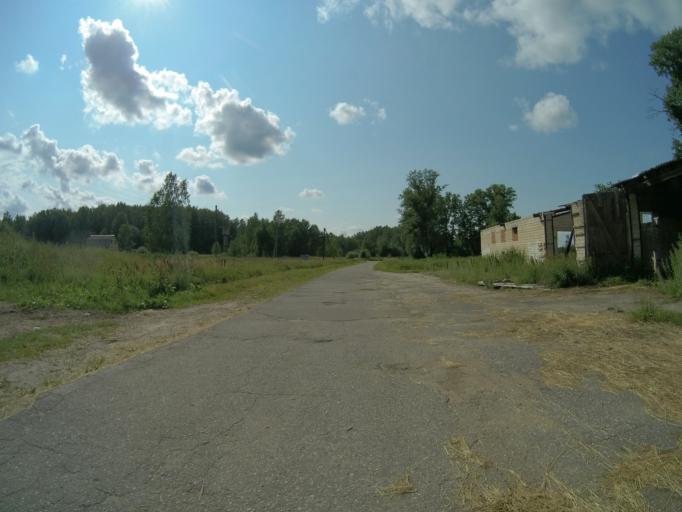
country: RU
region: Vladimir
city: Orgtrud
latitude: 56.2752
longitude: 40.6981
